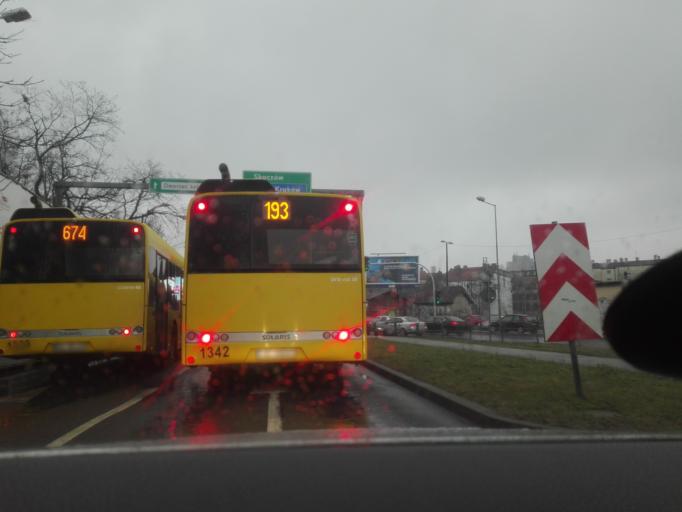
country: PL
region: Silesian Voivodeship
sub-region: Katowice
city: Katowice
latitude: 50.2587
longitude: 19.0118
